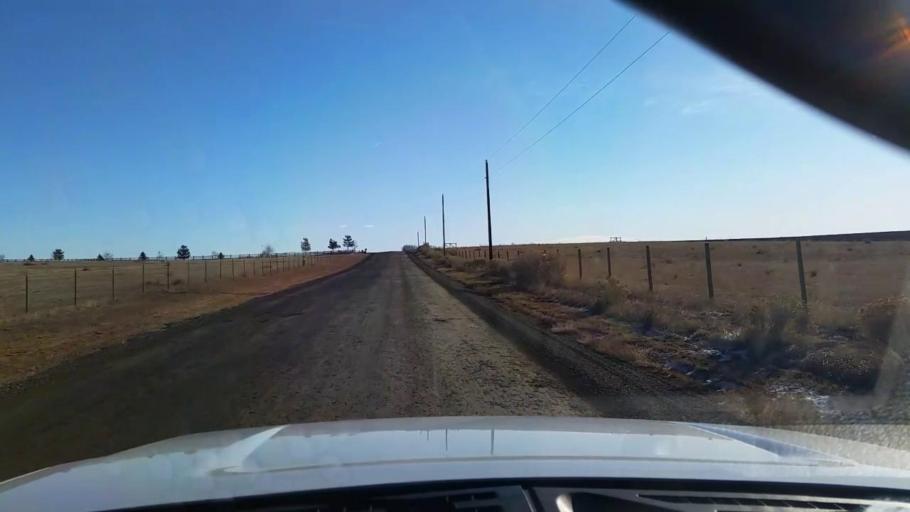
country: US
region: Colorado
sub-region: Larimer County
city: Wellington
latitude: 40.7696
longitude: -105.1096
